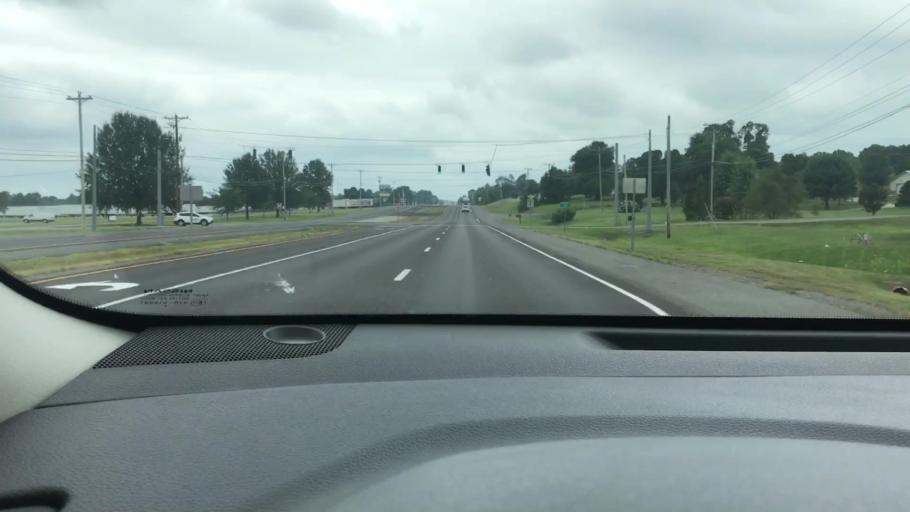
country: US
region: Kentucky
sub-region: Calloway County
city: Murray
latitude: 36.6596
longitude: -88.3058
